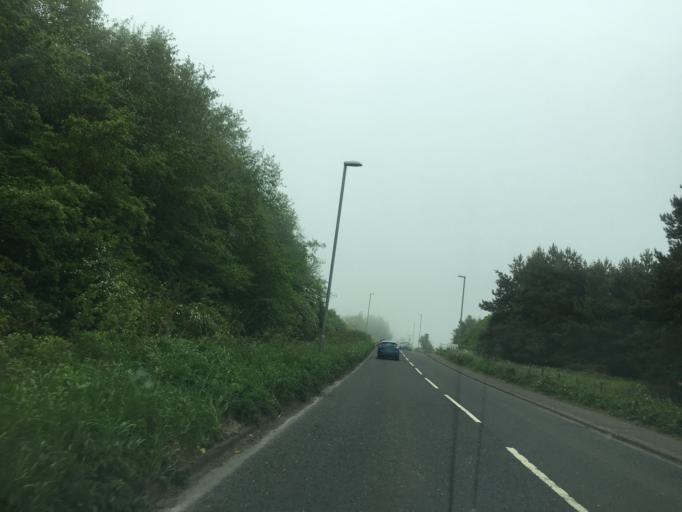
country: GB
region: Scotland
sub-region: Midlothian
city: Penicuik
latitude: 55.8499
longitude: -3.1911
